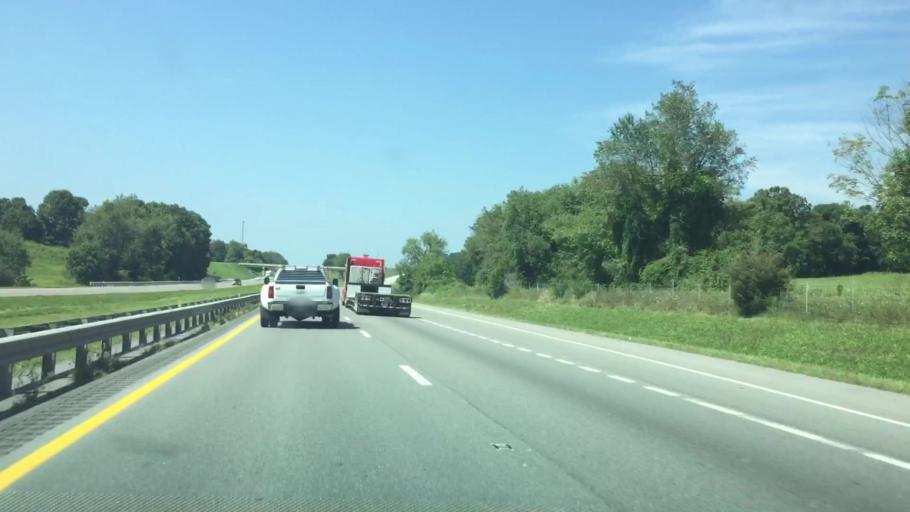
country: US
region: Virginia
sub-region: Washington County
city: Emory
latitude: 36.7677
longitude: -81.8278
